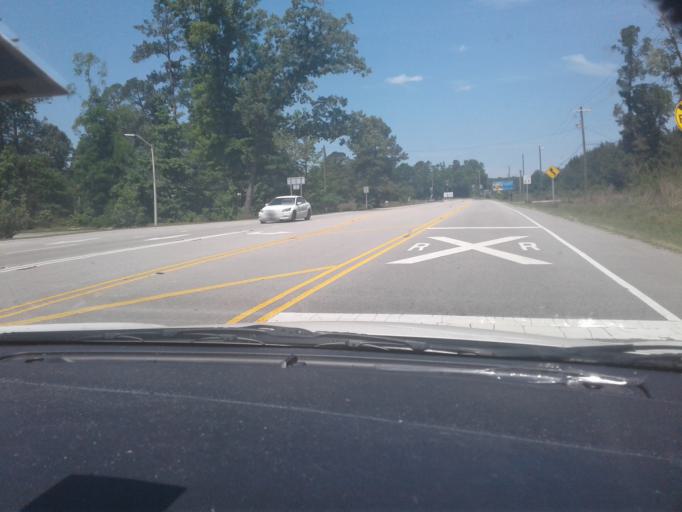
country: US
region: North Carolina
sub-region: Harnett County
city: Lillington
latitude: 35.4252
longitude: -78.8152
